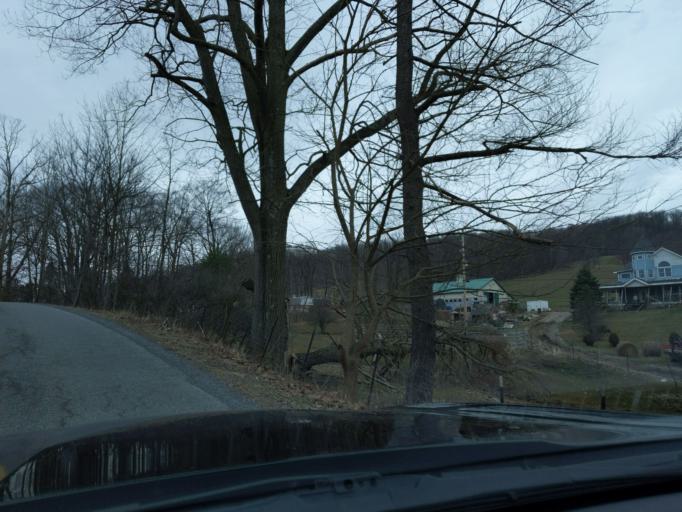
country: US
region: Pennsylvania
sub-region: Blair County
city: Bellwood
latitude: 40.5900
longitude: -78.3731
